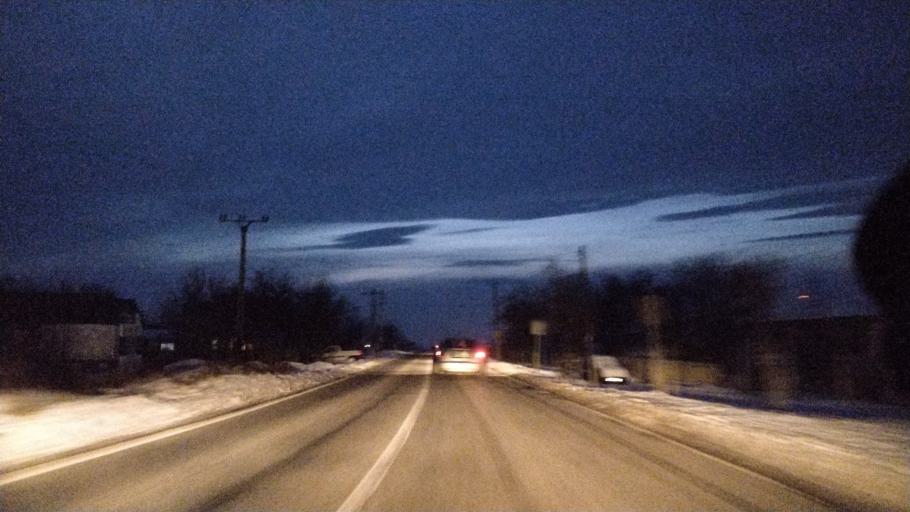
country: RO
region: Vrancea
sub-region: Comuna Milcovul
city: Milcovul
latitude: 45.6799
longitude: 27.2346
